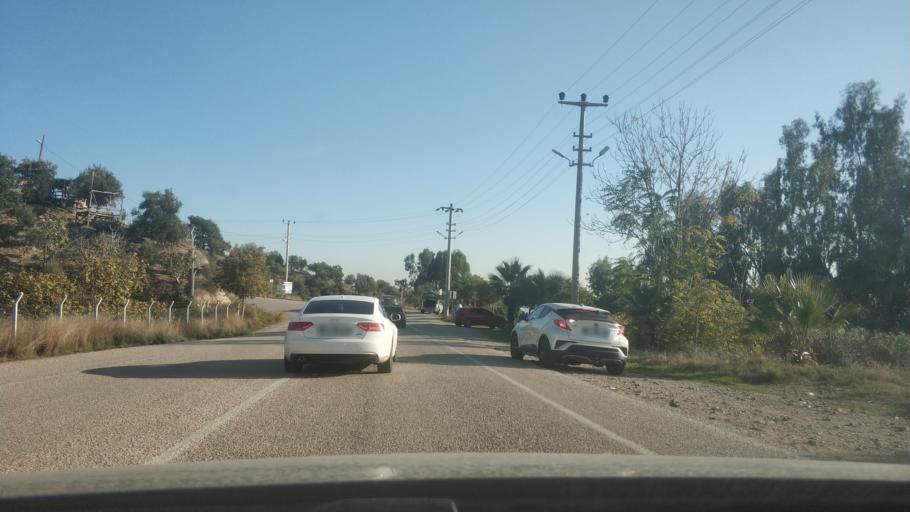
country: TR
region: Adana
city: Adana
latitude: 37.0989
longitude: 35.2869
